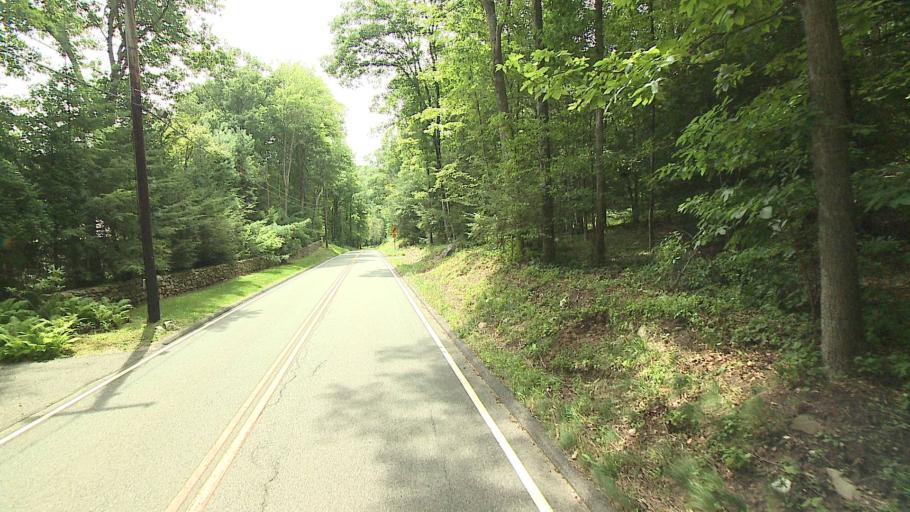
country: US
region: Connecticut
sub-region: Litchfield County
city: New Preston
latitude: 41.5963
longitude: -73.3200
